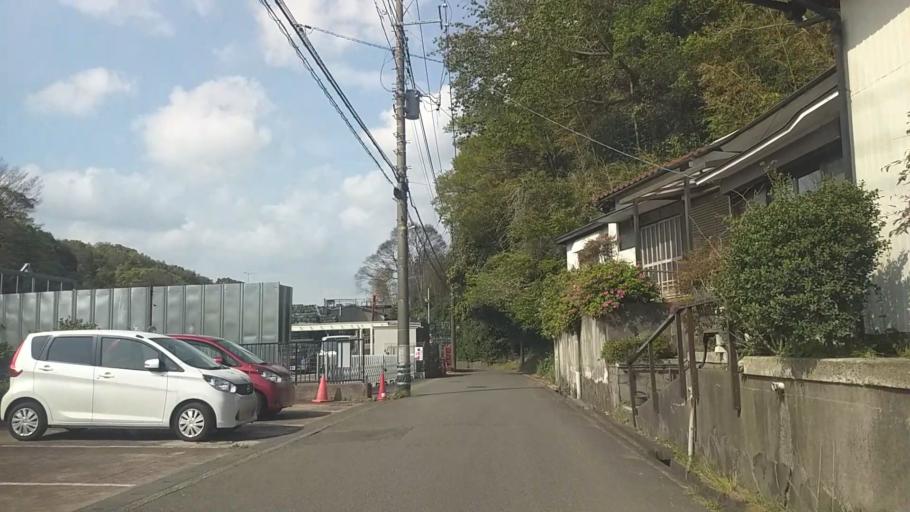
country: JP
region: Kanagawa
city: Kamakura
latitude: 35.3814
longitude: 139.5642
